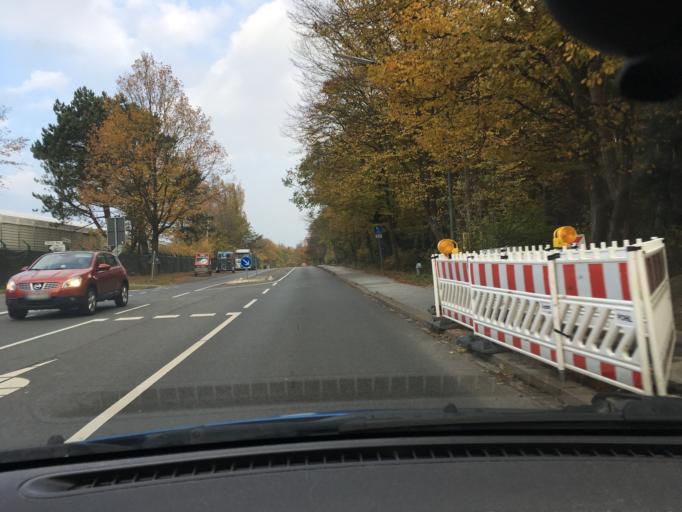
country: DE
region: Schleswig-Holstein
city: Flensburg
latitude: 54.8140
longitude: 9.4219
